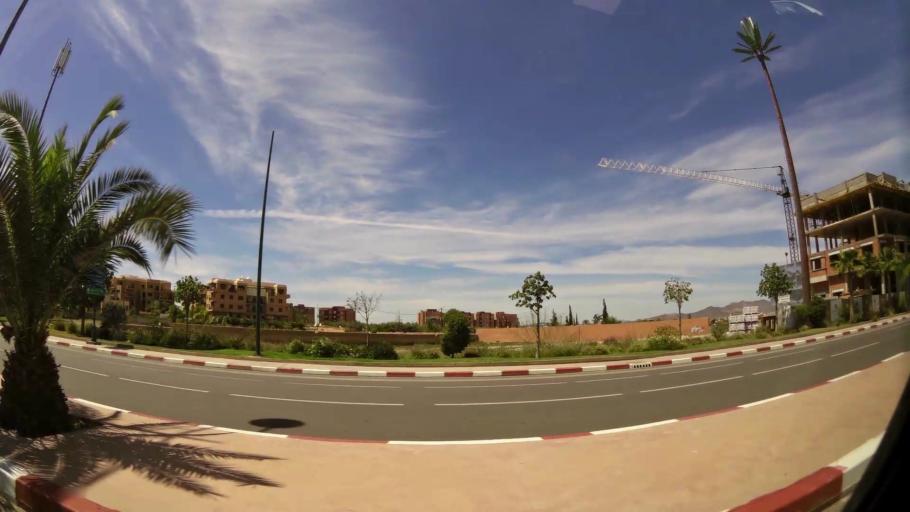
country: MA
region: Marrakech-Tensift-Al Haouz
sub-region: Marrakech
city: Marrakesh
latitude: 31.6721
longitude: -8.0065
